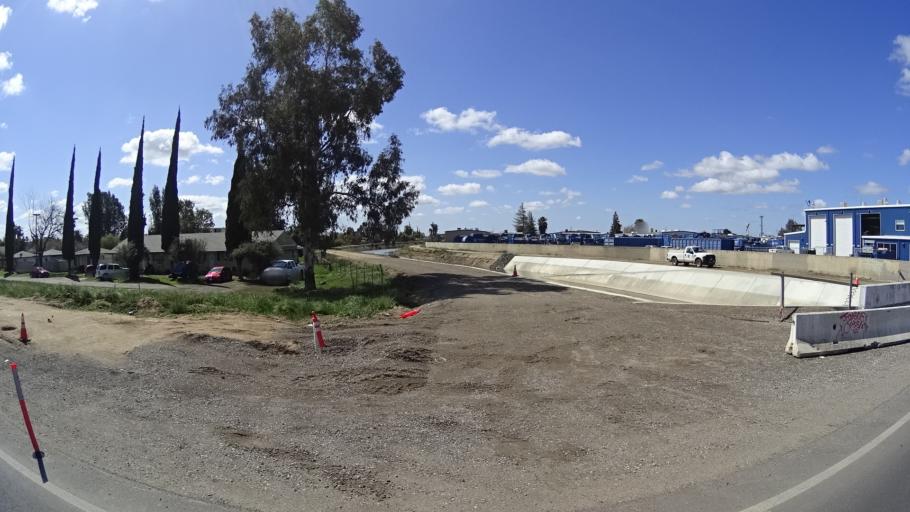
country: US
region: California
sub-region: Fresno County
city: West Park
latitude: 36.8146
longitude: -119.8871
